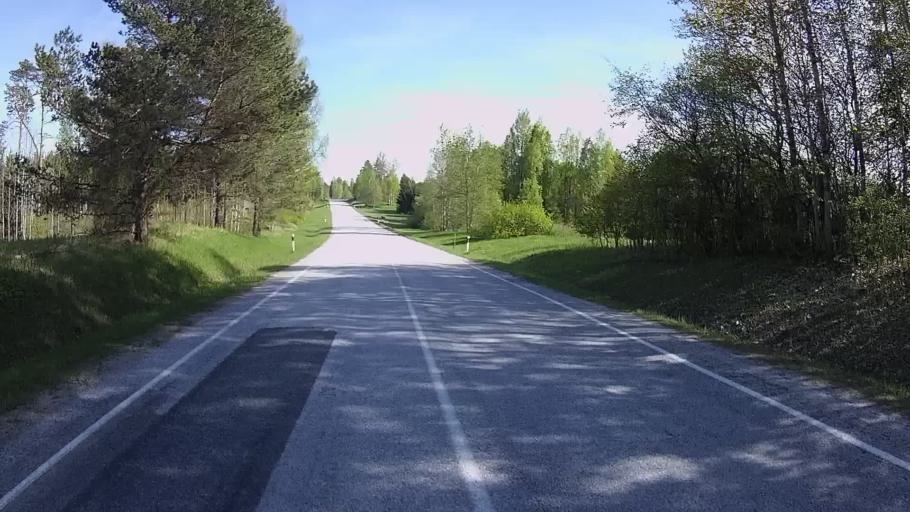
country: EE
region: Vorumaa
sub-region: Antsla vald
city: Vana-Antsla
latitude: 58.0090
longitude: 26.4956
